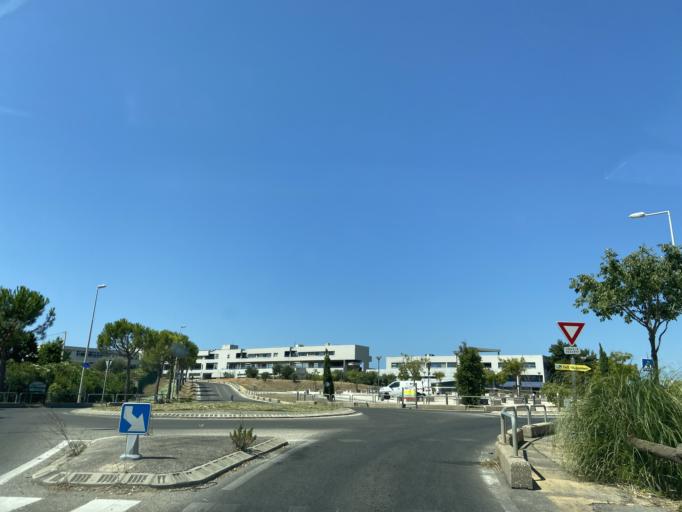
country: FR
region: Provence-Alpes-Cote d'Azur
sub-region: Departement des Bouches-du-Rhone
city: Plan-de-Cuques
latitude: 43.3436
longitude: 5.4403
